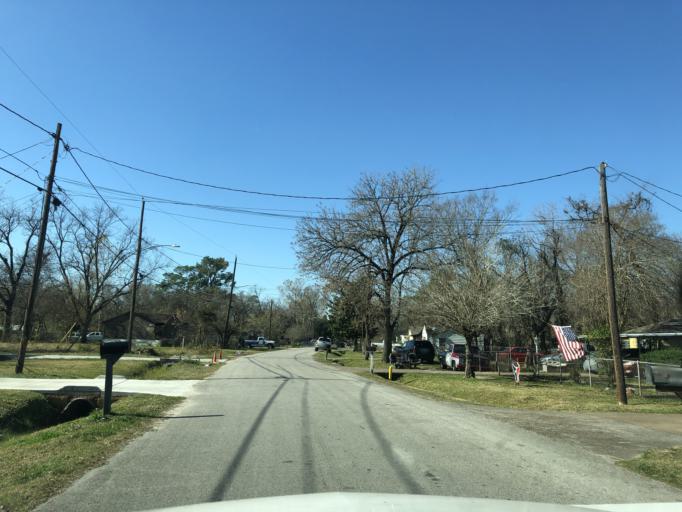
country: US
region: Texas
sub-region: Harris County
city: Jacinto City
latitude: 29.8386
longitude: -95.2916
